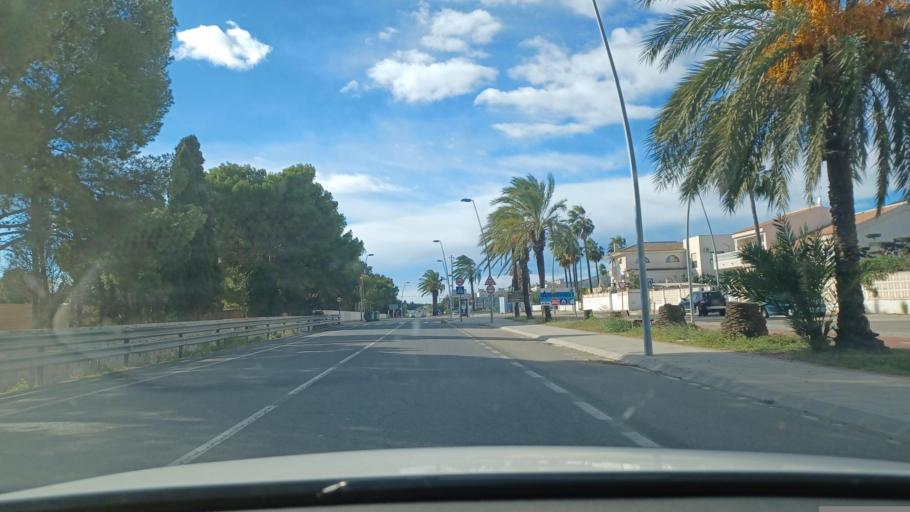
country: ES
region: Catalonia
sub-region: Provincia de Tarragona
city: Sant Carles de la Rapita
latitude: 40.5964
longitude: 0.5712
